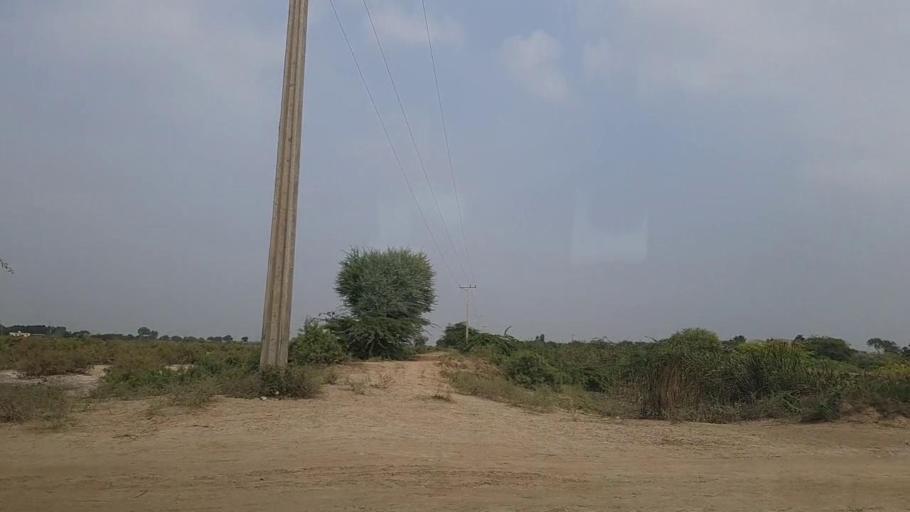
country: PK
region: Sindh
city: Mirpur Sakro
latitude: 24.6131
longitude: 67.7179
